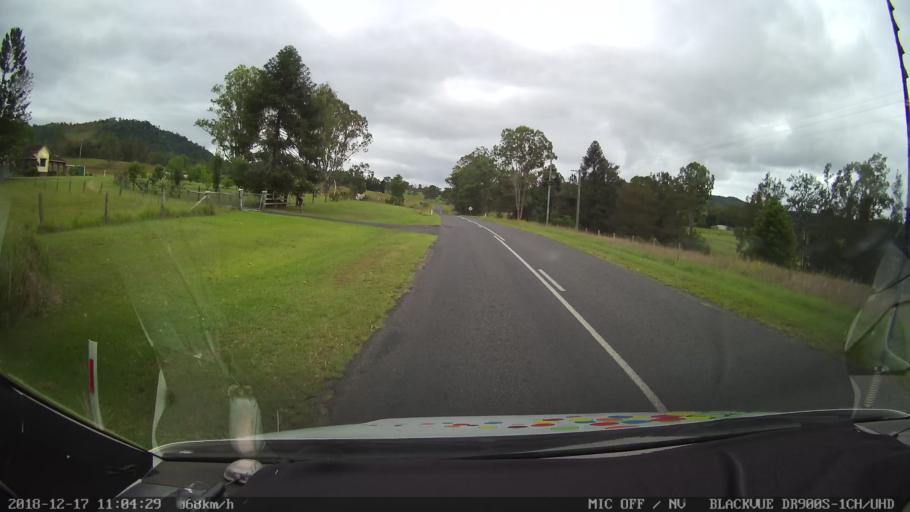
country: AU
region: New South Wales
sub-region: Kyogle
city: Kyogle
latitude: -28.7984
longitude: 152.6428
